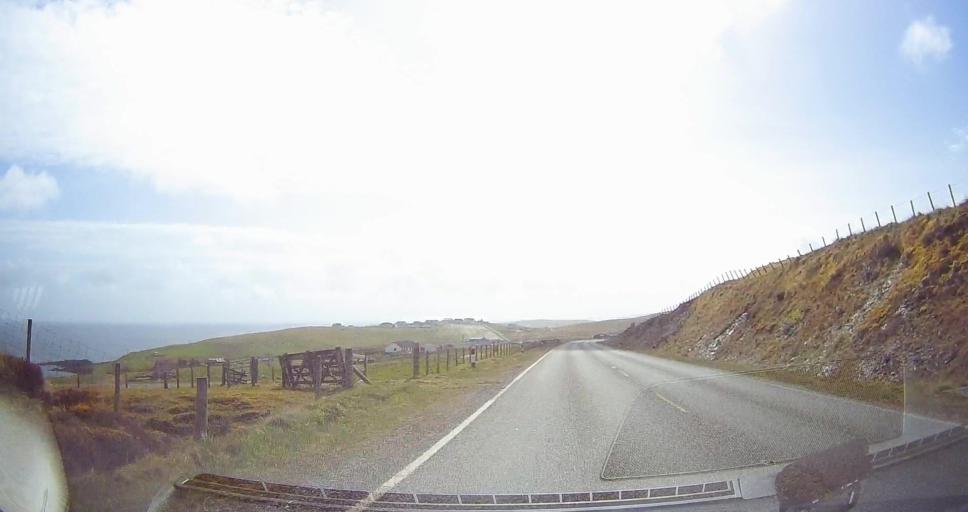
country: GB
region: Scotland
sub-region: Shetland Islands
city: Sandwick
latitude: 60.0667
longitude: -1.2244
